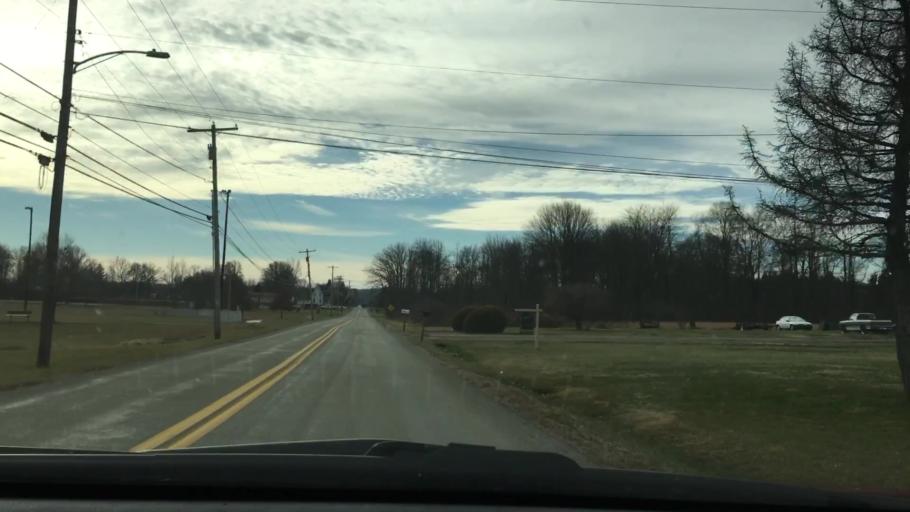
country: US
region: Pennsylvania
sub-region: Greene County
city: Fairdale
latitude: 39.8870
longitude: -79.9763
